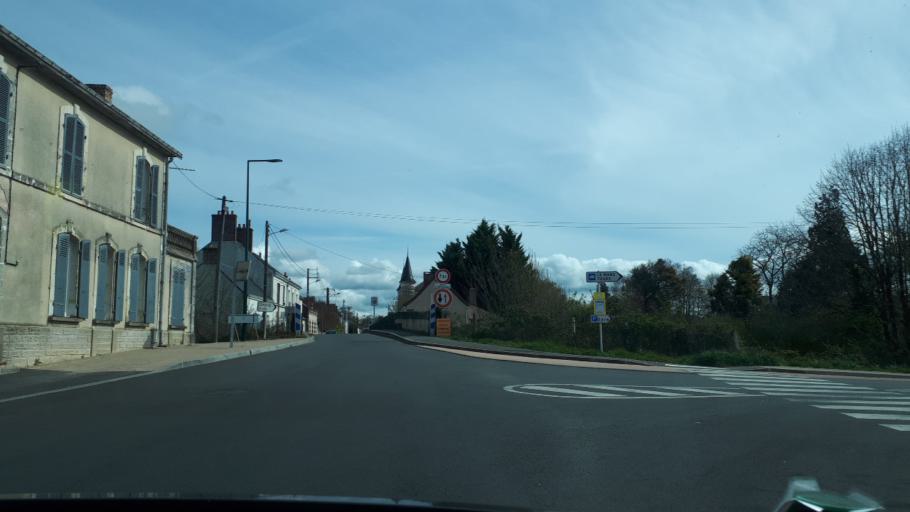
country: FR
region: Pays de la Loire
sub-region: Departement de la Sarthe
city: Ecommoy
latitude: 47.8258
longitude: 0.2662
